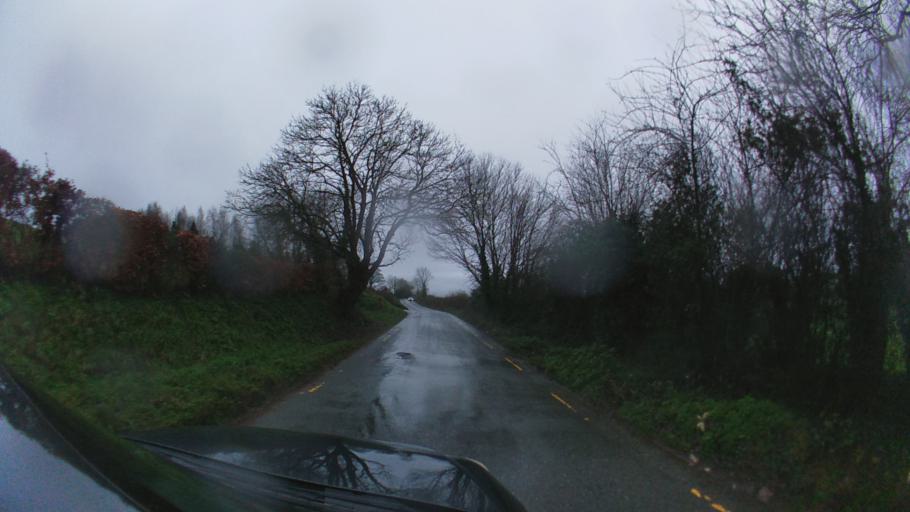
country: IE
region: Leinster
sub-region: Kilkenny
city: Graiguenamanagh
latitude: 52.6133
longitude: -6.9901
